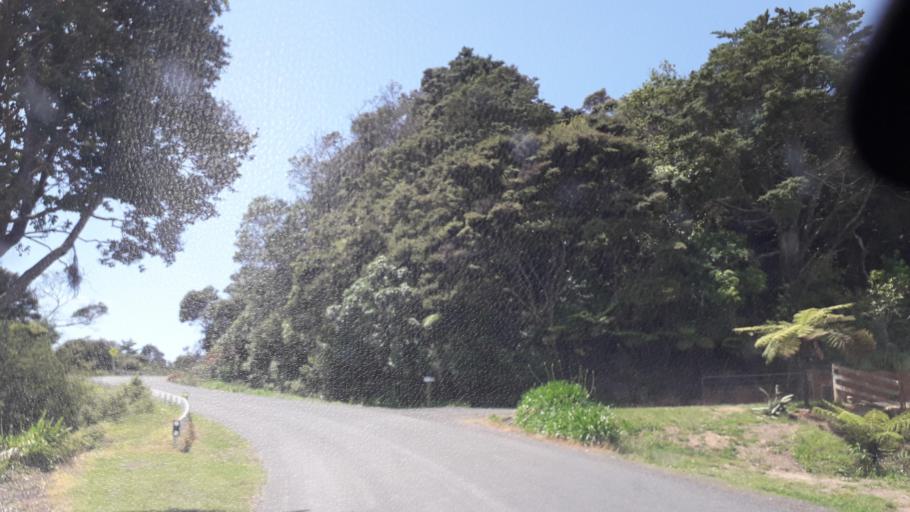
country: NZ
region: Northland
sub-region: Far North District
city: Paihia
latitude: -35.2357
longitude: 174.2605
